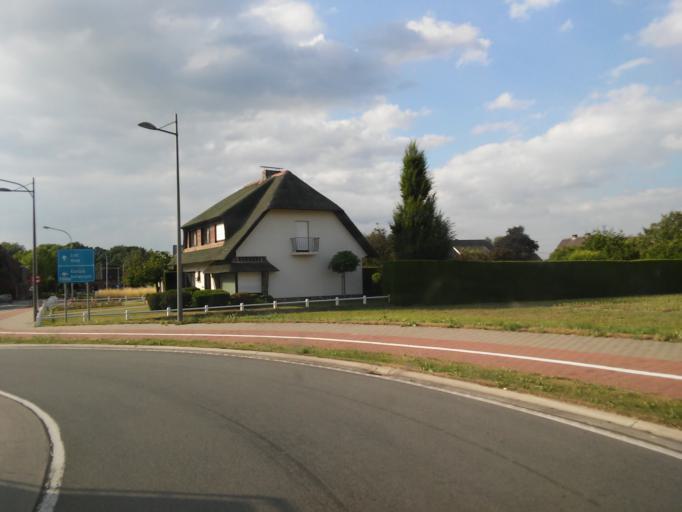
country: BE
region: Flanders
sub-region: Provincie Antwerpen
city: Duffel
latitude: 51.1052
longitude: 4.4961
